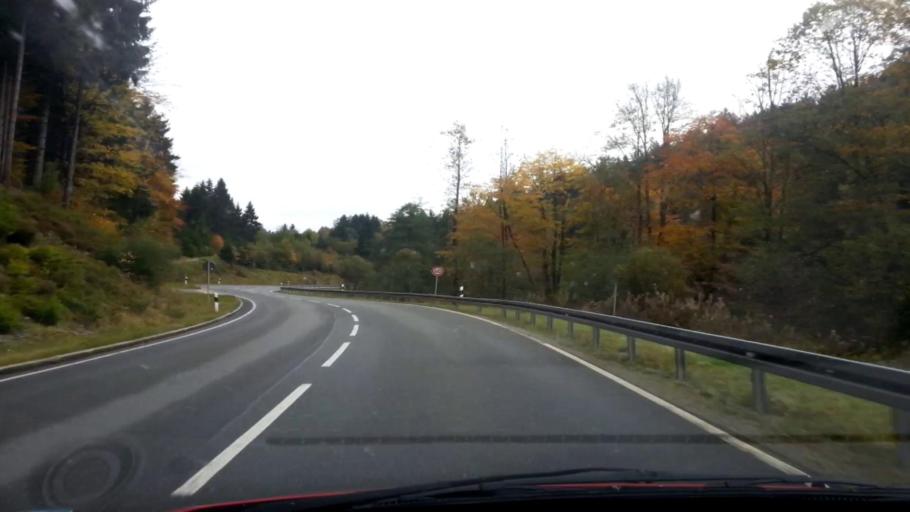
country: DE
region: Bavaria
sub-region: Upper Franconia
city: Warmensteinach
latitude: 49.9789
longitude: 11.7673
